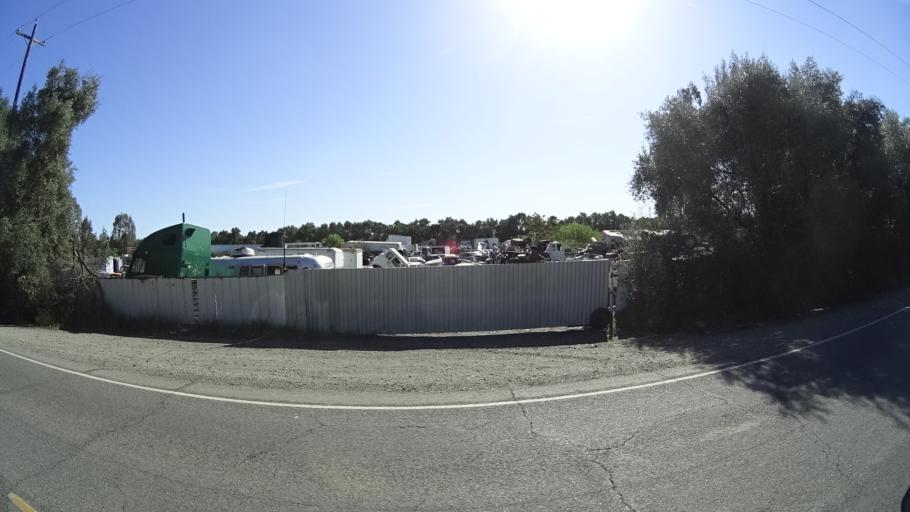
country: US
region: California
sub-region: Glenn County
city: Orland
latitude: 39.7045
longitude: -122.1969
